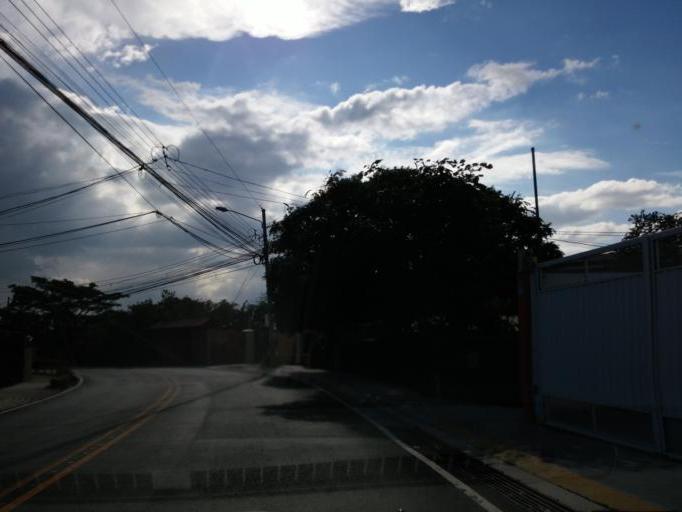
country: CR
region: Heredia
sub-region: Canton de Belen
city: San Antonio
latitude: 9.9812
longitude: -84.1926
